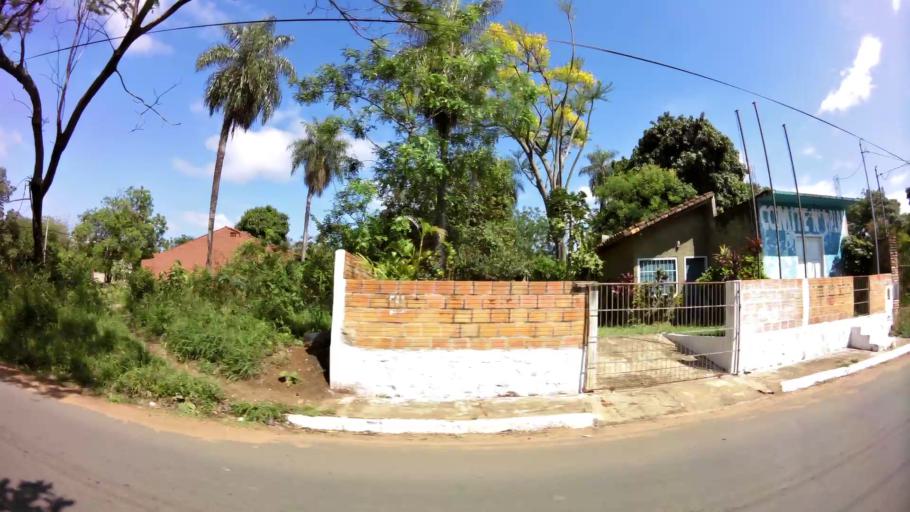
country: PY
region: Central
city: San Lorenzo
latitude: -25.2558
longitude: -57.4936
